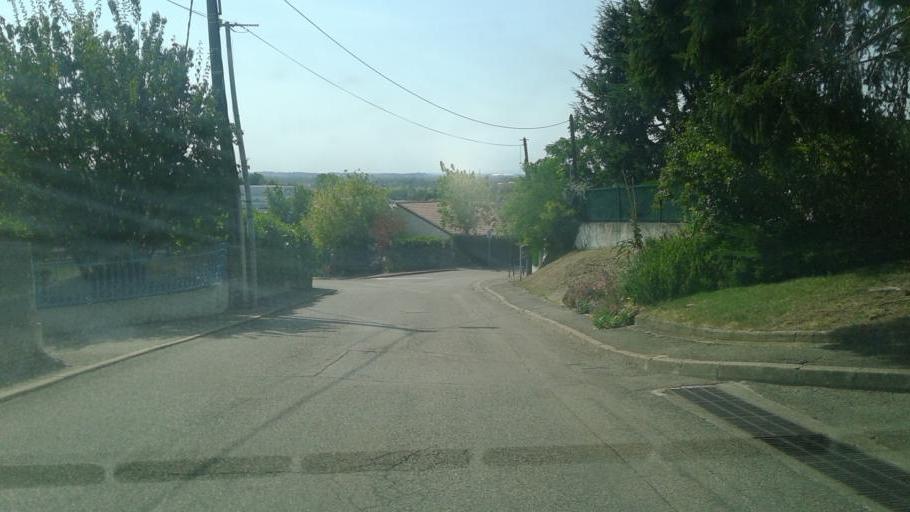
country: FR
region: Rhone-Alpes
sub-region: Departement de l'Ain
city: Montluel
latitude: 45.8505
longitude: 5.0491
